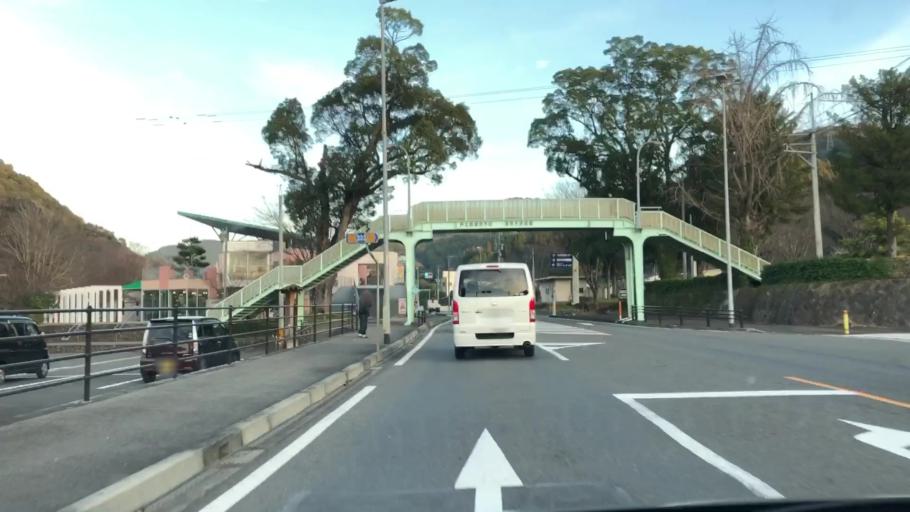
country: JP
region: Kumamoto
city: Minamata
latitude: 32.2317
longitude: 130.4560
